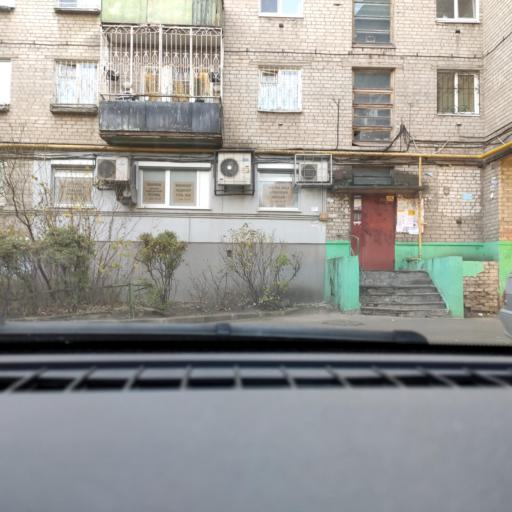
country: RU
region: Voronezj
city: Voronezh
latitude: 51.6823
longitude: 39.2608
